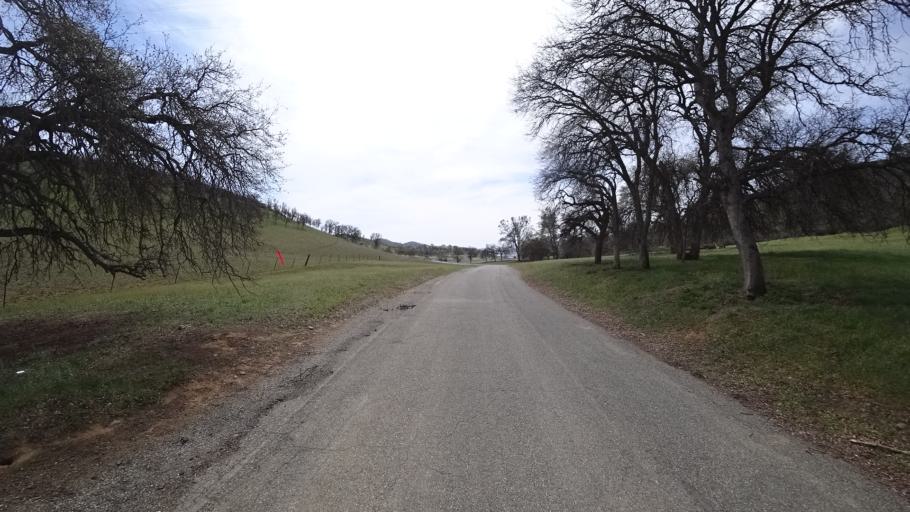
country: US
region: California
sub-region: Glenn County
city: Willows
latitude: 39.5975
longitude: -122.5278
